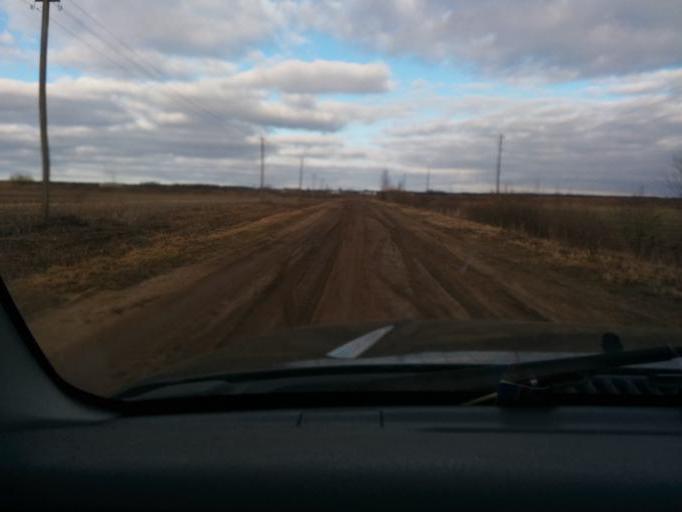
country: LV
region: Jelgava
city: Jelgava
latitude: 56.6902
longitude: 23.6814
